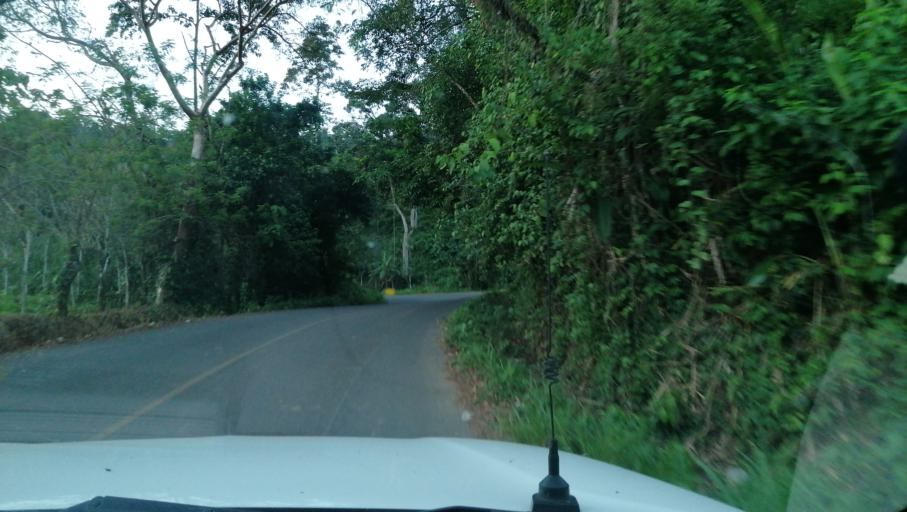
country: MX
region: Chiapas
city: Ostuacan
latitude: 17.4238
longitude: -93.3374
